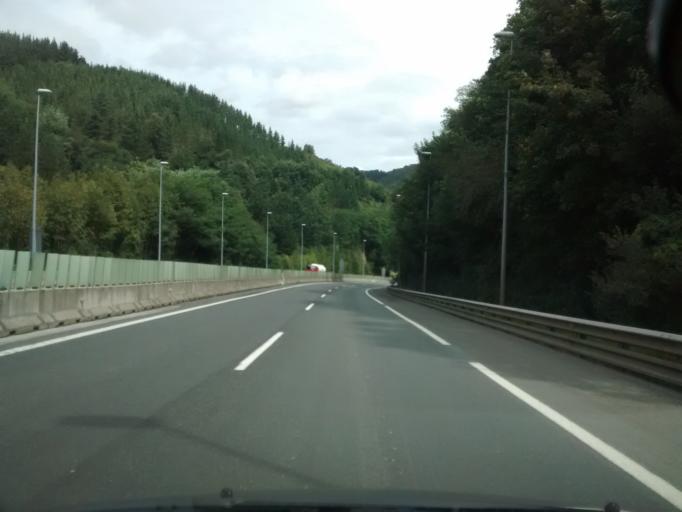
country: ES
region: Basque Country
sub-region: Bizkaia
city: Ermua
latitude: 43.1753
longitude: -2.5054
